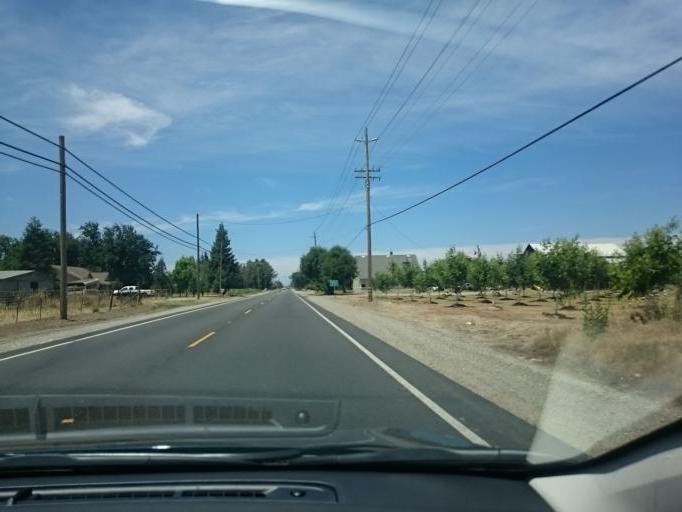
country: US
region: California
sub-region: Stanislaus County
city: Hughson
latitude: 37.6388
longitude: -120.8361
